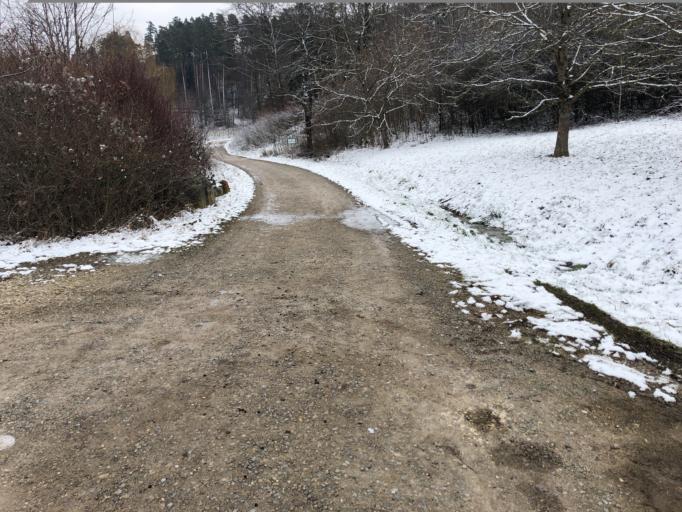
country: DE
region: Baden-Wuerttemberg
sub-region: Tuebingen Region
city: Nehren
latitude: 48.4159
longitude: 9.0723
